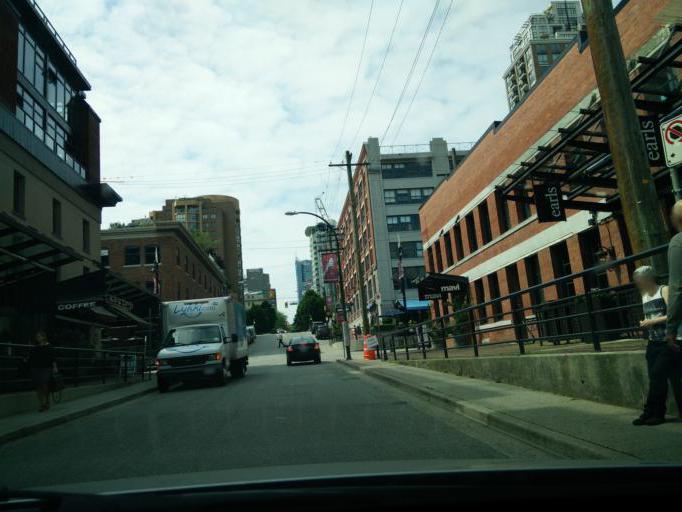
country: CA
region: British Columbia
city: West End
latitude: 49.2757
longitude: -123.1207
